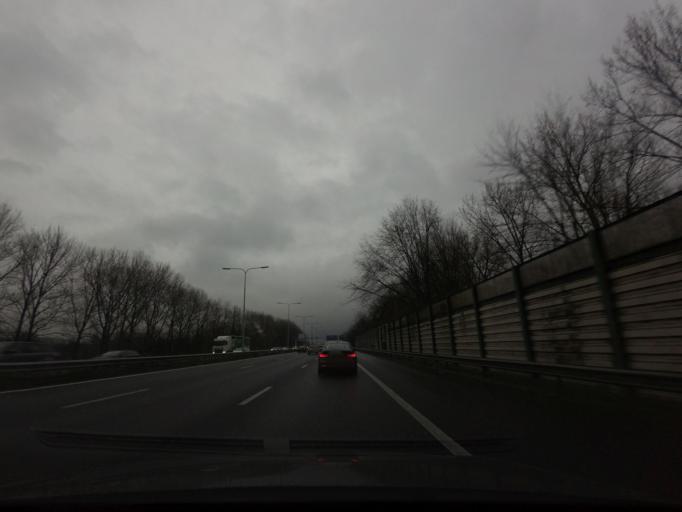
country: NL
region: South Holland
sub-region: Gemeente Delft
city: Delft
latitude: 52.0183
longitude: 4.3696
